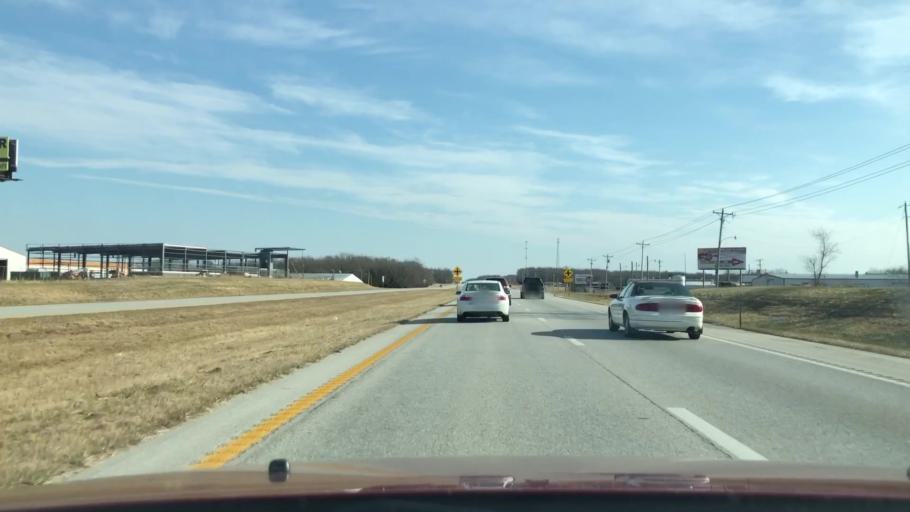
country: US
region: Missouri
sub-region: Webster County
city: Rogersville
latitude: 37.1150
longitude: -93.0323
